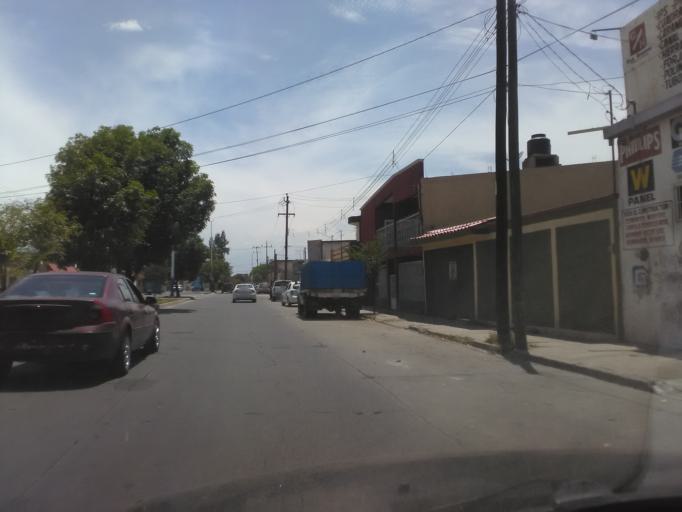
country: MX
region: Durango
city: Victoria de Durango
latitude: 24.0211
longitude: -104.6269
